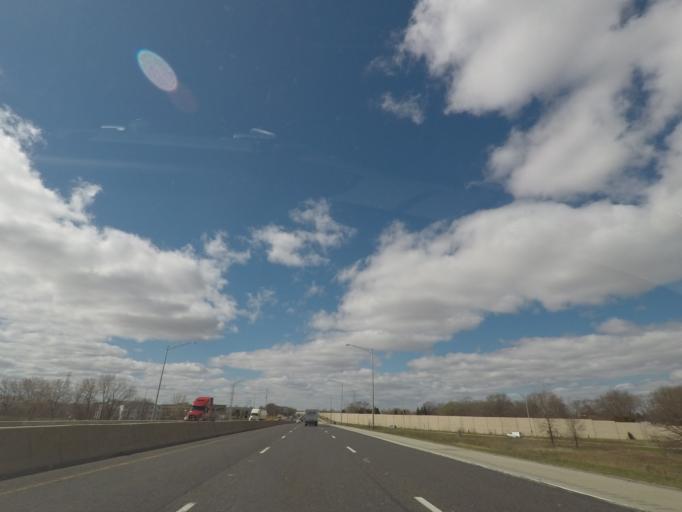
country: US
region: Illinois
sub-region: Will County
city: Crystal Lawns
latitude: 41.5832
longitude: -88.1695
